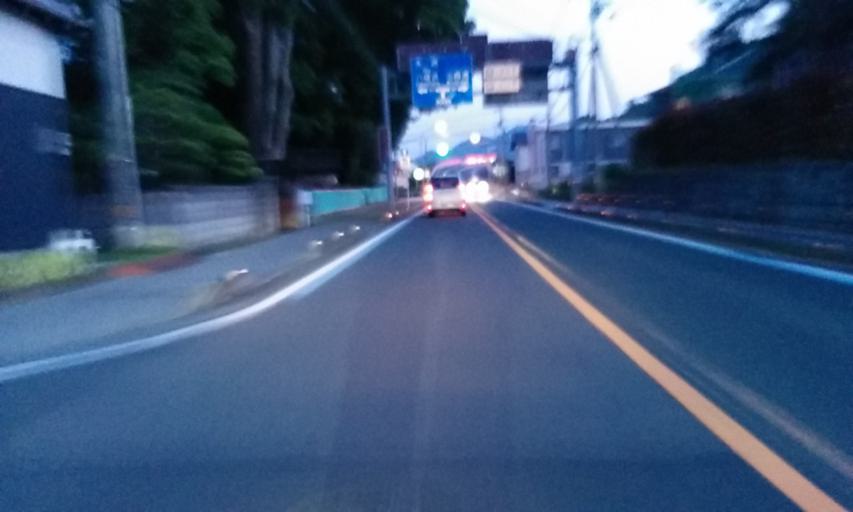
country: JP
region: Ehime
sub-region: Nishiuwa-gun
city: Ikata-cho
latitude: 33.4913
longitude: 132.3975
